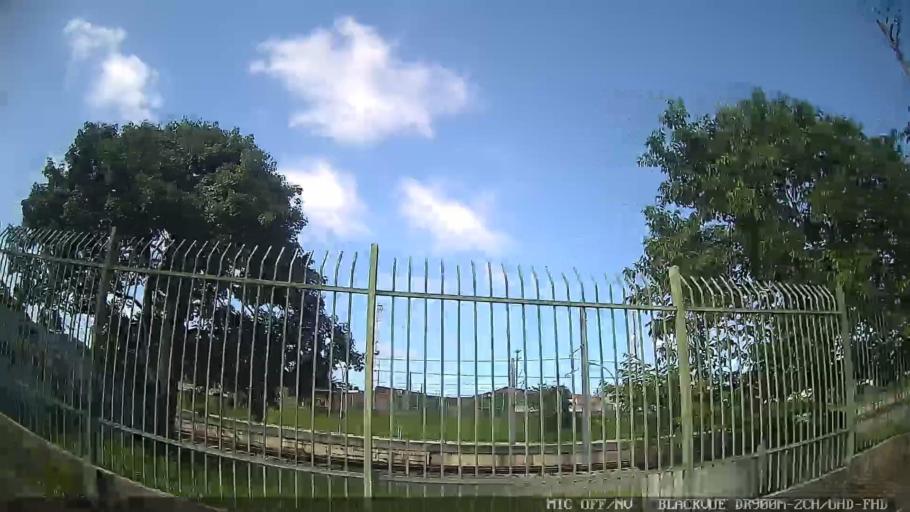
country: BR
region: Sao Paulo
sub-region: Itaquaquecetuba
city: Itaquaquecetuba
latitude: -23.4861
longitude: -46.3473
